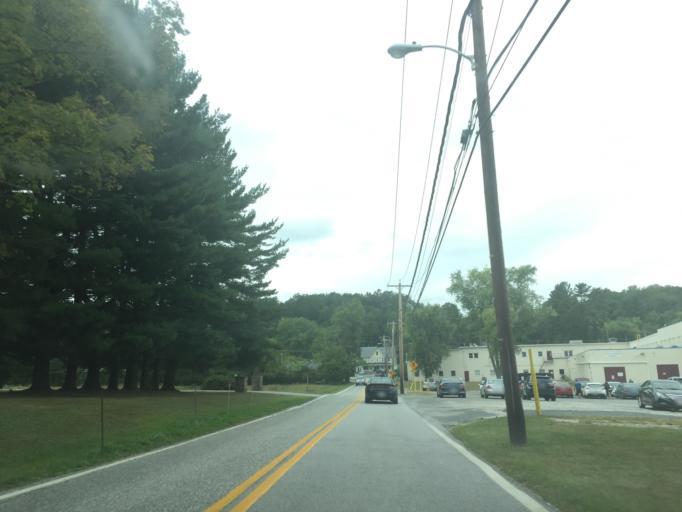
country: US
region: Maryland
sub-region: Baltimore County
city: Perry Hall
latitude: 39.4549
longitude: -76.4960
